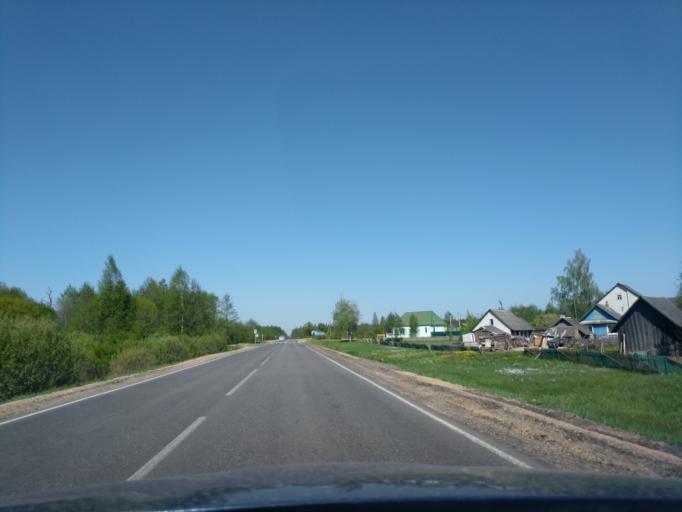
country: BY
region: Minsk
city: Il'ya
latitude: 54.3969
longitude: 27.3364
